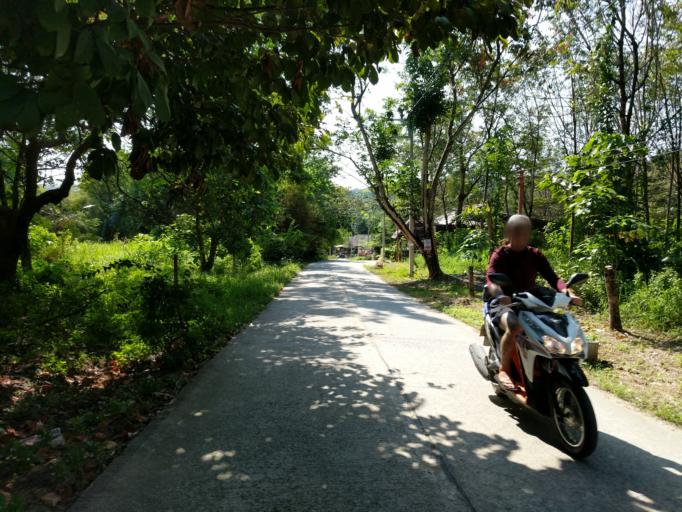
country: TH
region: Ranong
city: Kapoe
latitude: 9.7414
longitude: 98.4164
